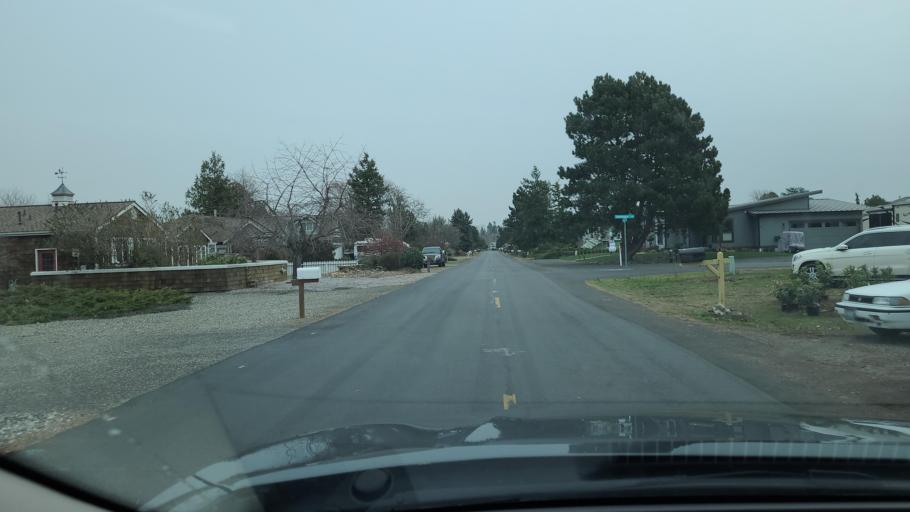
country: US
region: Washington
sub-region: Whatcom County
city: Birch Bay
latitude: 48.9365
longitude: -122.7821
